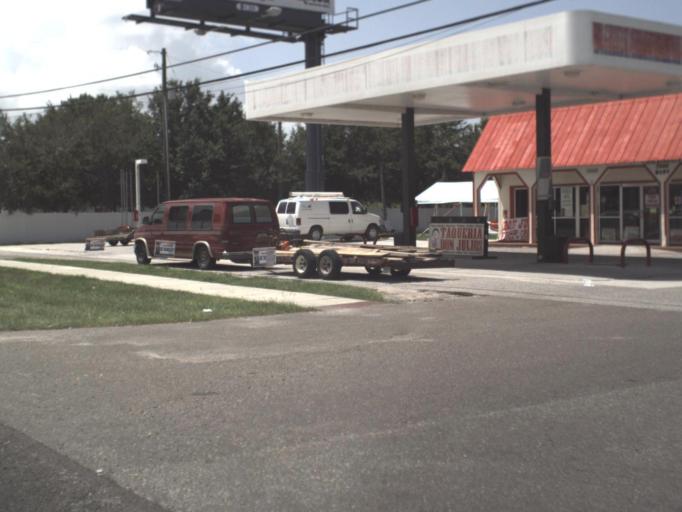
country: US
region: Florida
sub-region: Hillsborough County
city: Riverview
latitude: 27.7971
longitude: -82.3350
